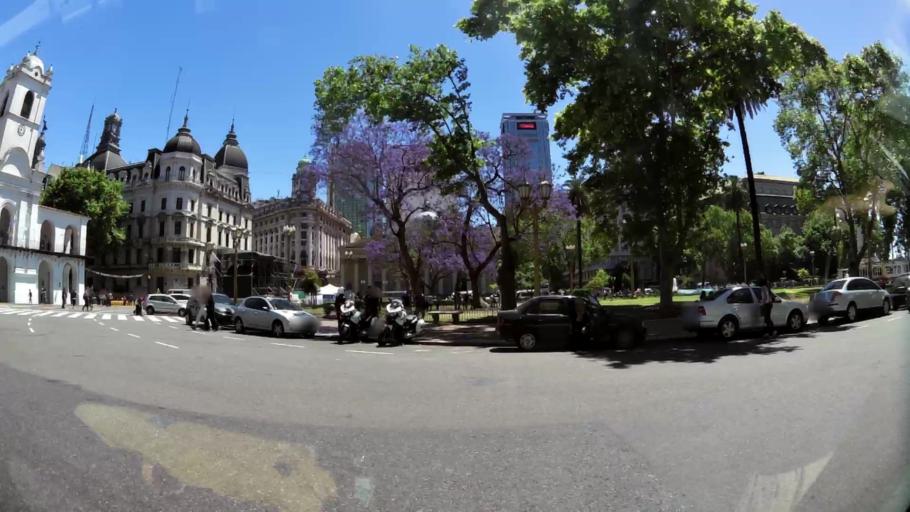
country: AR
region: Buenos Aires F.D.
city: Buenos Aires
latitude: -34.6088
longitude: -58.3731
